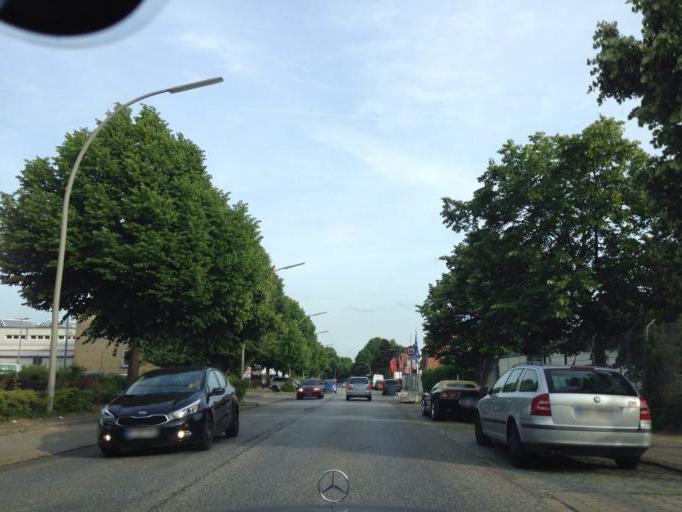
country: DE
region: Hamburg
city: Steilshoop
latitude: 53.5989
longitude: 10.0705
